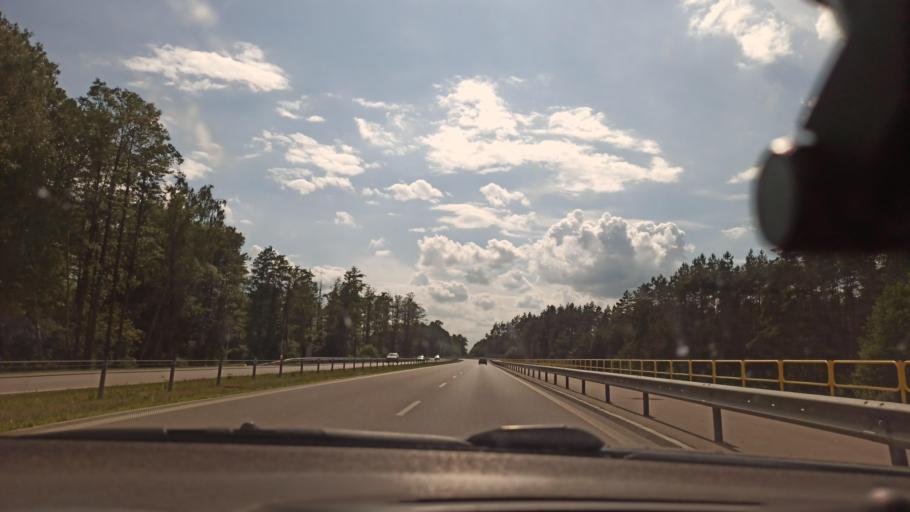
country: PL
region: Podlasie
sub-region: Powiat bialostocki
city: Turosn Koscielna
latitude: 53.0650
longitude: 23.0703
